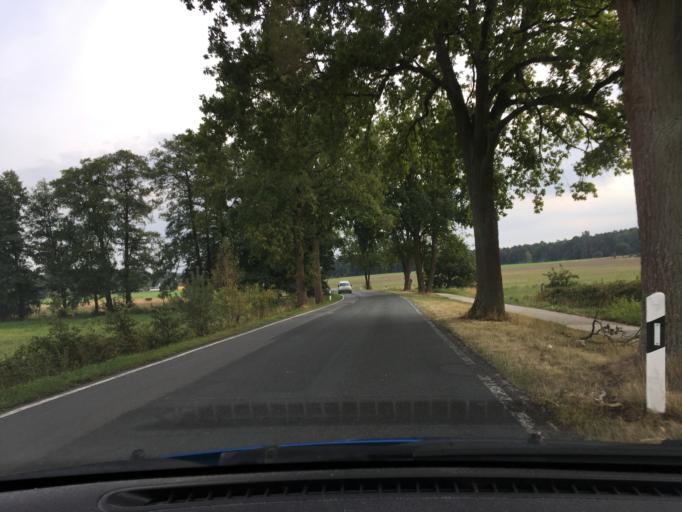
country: DE
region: Lower Saxony
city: Asendorf
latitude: 53.2745
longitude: 9.9736
